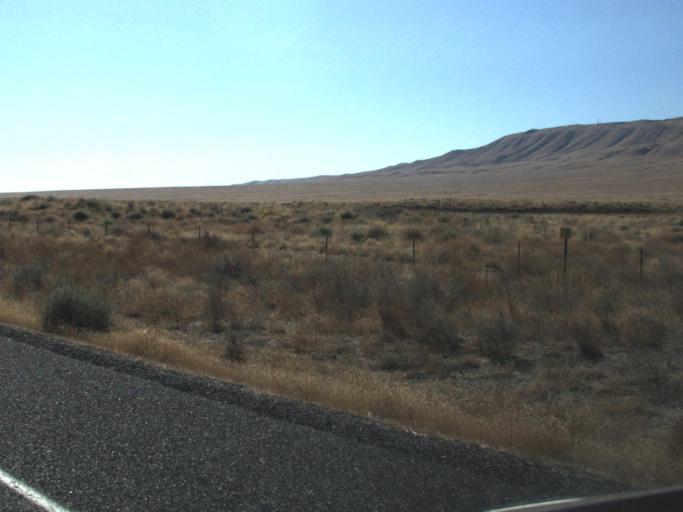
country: US
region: Washington
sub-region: Benton County
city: Benton City
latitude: 46.4986
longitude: -119.6086
